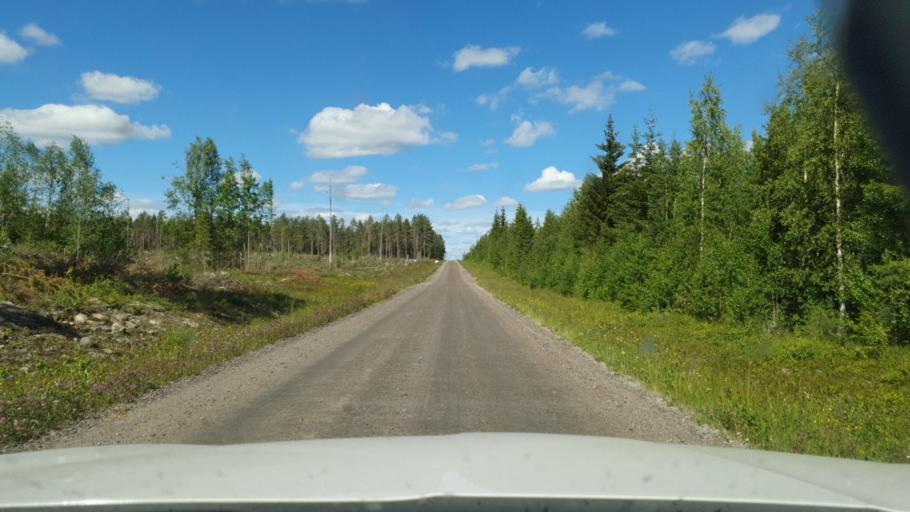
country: SE
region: Vaesterbotten
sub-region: Skelleftea Kommun
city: Byske
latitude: 65.1307
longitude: 21.1979
